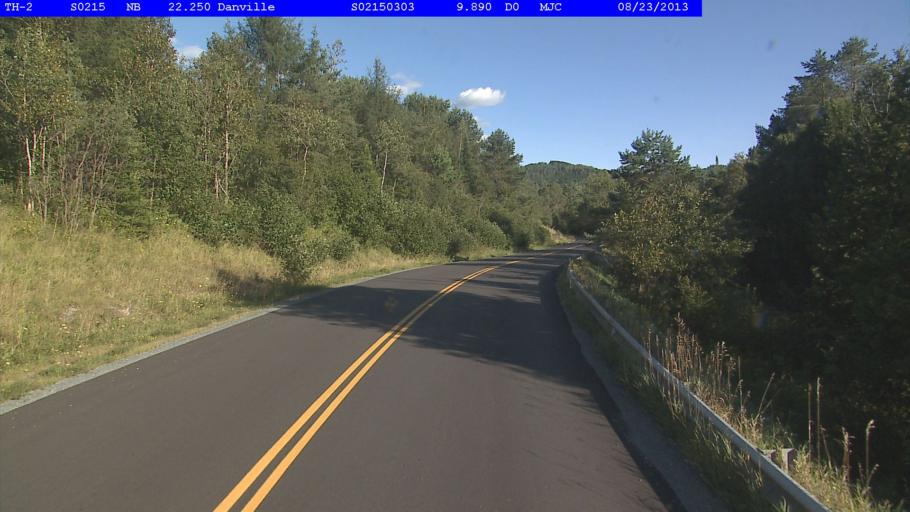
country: US
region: Vermont
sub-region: Caledonia County
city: St Johnsbury
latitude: 44.4509
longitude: -72.0674
